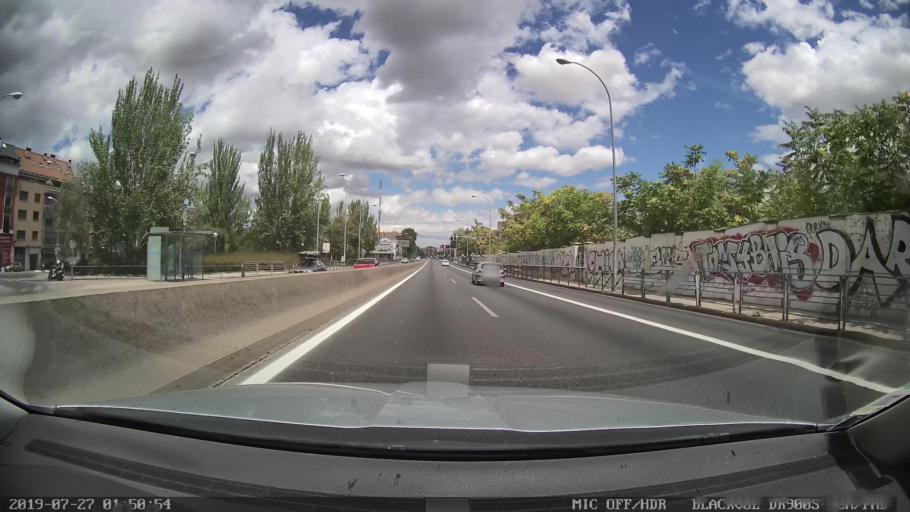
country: ES
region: Madrid
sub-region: Provincia de Madrid
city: Latina
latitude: 40.3929
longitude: -3.7727
